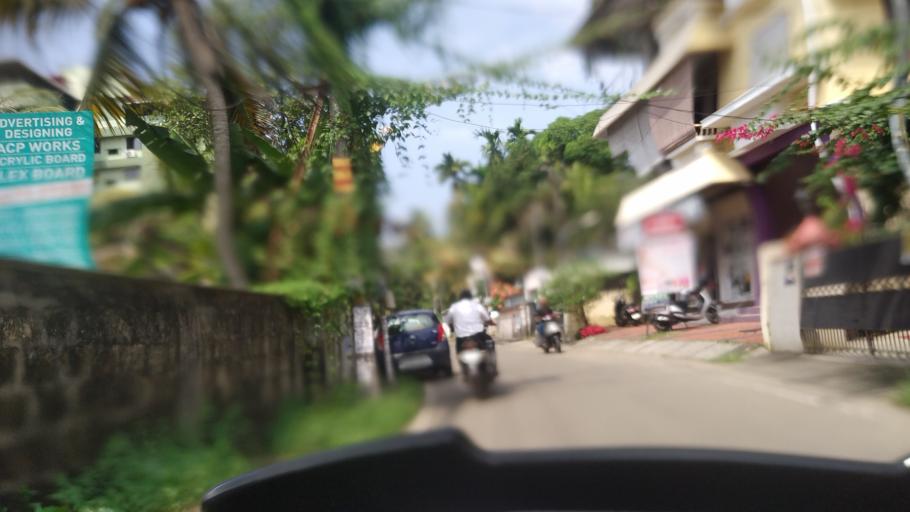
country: IN
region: Kerala
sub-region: Ernakulam
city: Cochin
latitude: 9.9883
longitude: 76.2977
